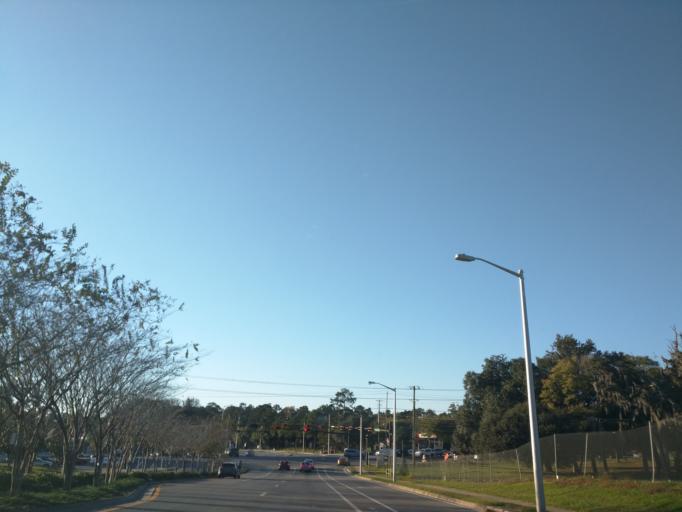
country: US
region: Florida
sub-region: Leon County
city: Tallahassee
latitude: 30.4409
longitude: -84.2254
